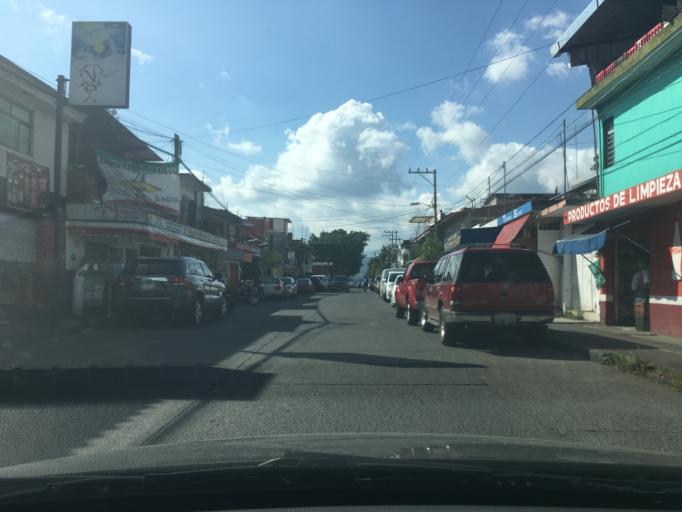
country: MX
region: Michoacan
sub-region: Uruapan
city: Uruapan
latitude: 19.4085
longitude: -102.0503
